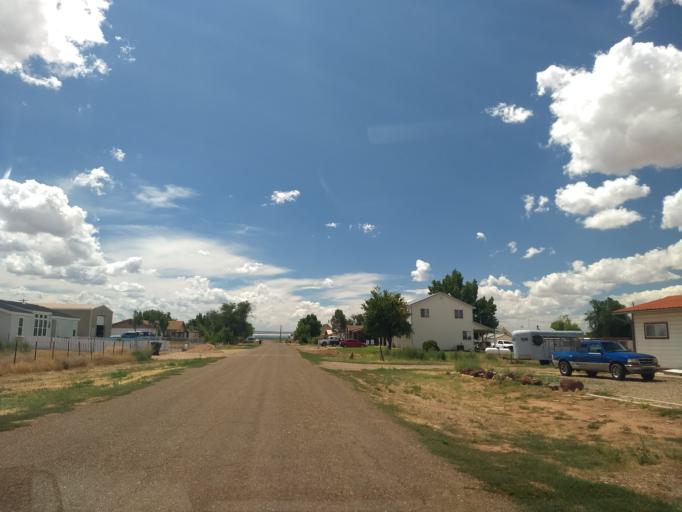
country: US
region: Arizona
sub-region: Coconino County
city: Fredonia
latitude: 36.9430
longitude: -112.5206
